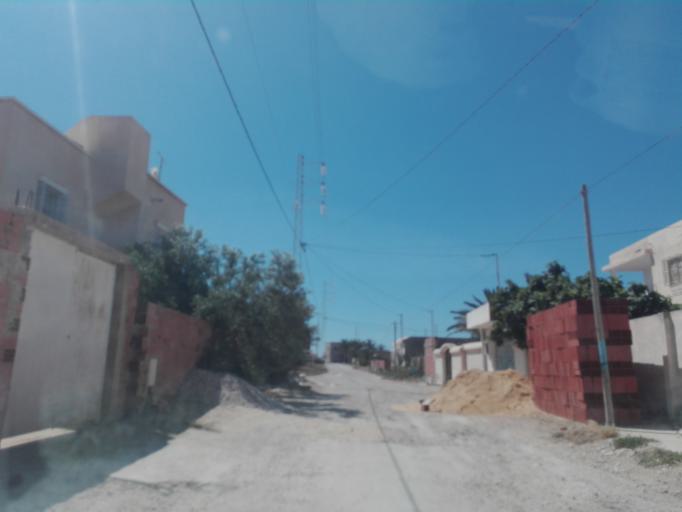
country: TN
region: Safaqis
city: Jabinyanah
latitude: 34.7413
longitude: 11.2983
